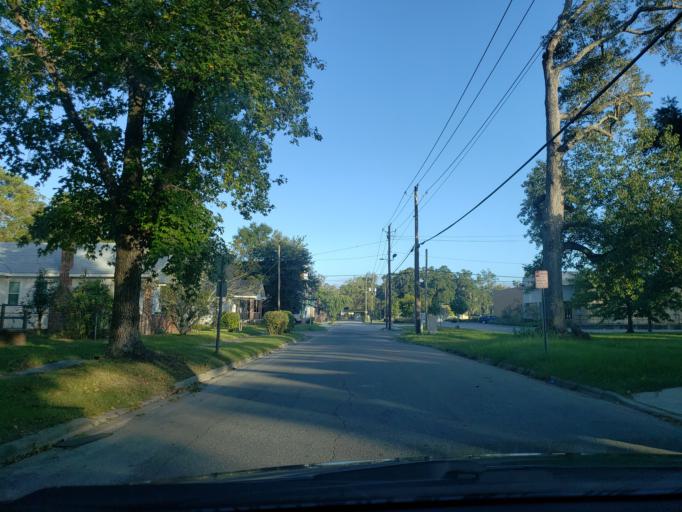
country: US
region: Georgia
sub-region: Chatham County
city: Savannah
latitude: 32.0543
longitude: -81.0850
